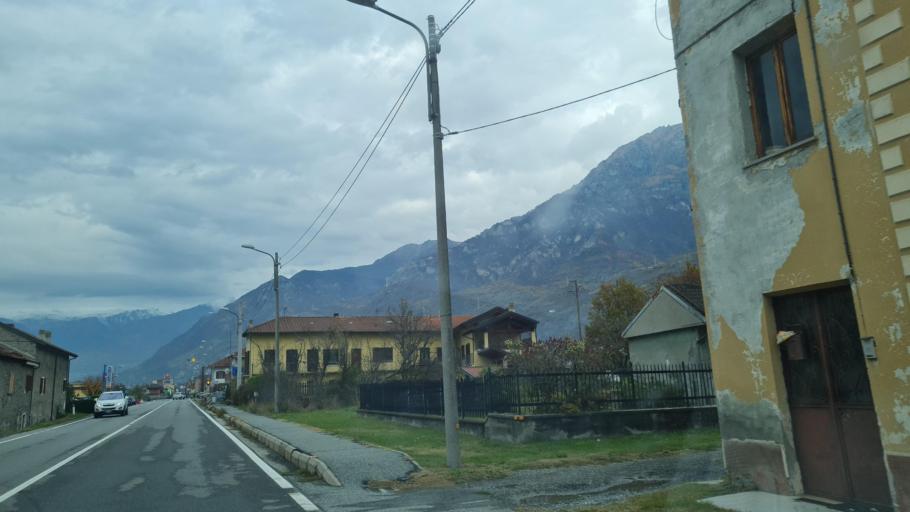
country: IT
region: Piedmont
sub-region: Provincia di Torino
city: Chianocco
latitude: 45.1370
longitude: 7.1653
